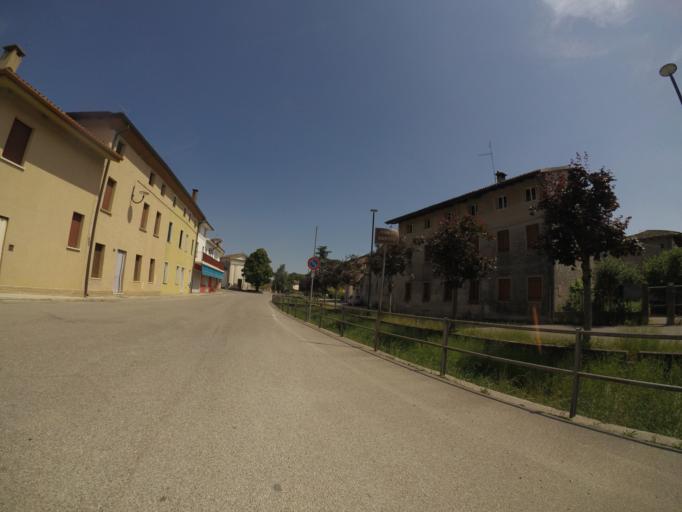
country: IT
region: Friuli Venezia Giulia
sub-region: Provincia di Udine
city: Camino al Tagliamento
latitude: 45.9390
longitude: 12.9373
